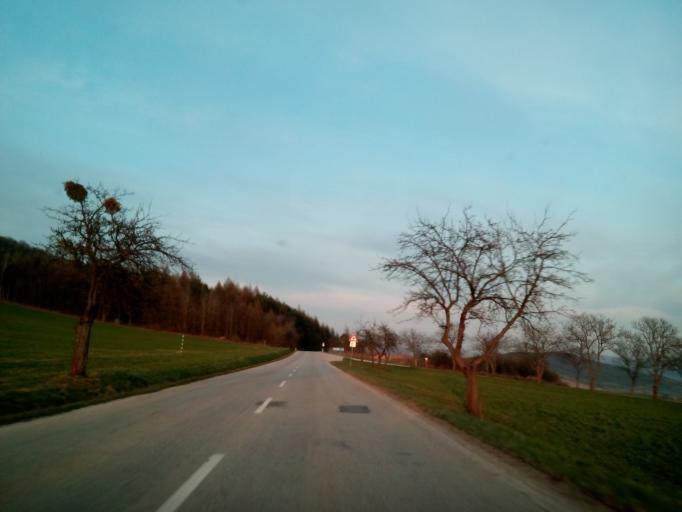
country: SK
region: Kosicky
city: Roznava
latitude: 48.6598
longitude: 20.4694
